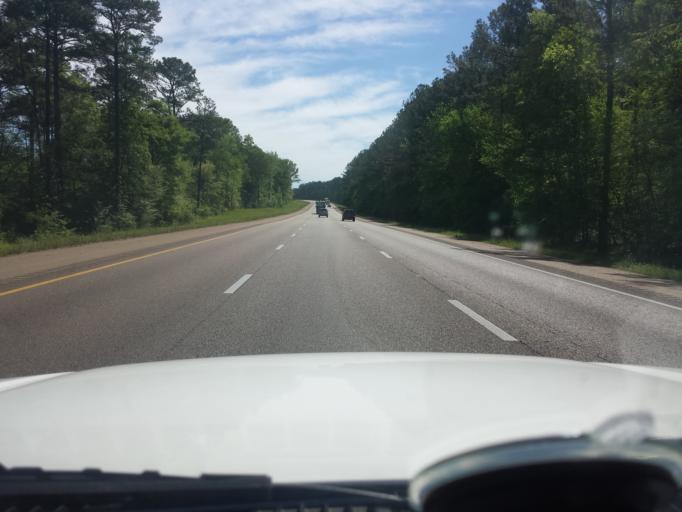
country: US
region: Mississippi
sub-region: Rankin County
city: Pearl
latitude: 32.2661
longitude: -90.1135
